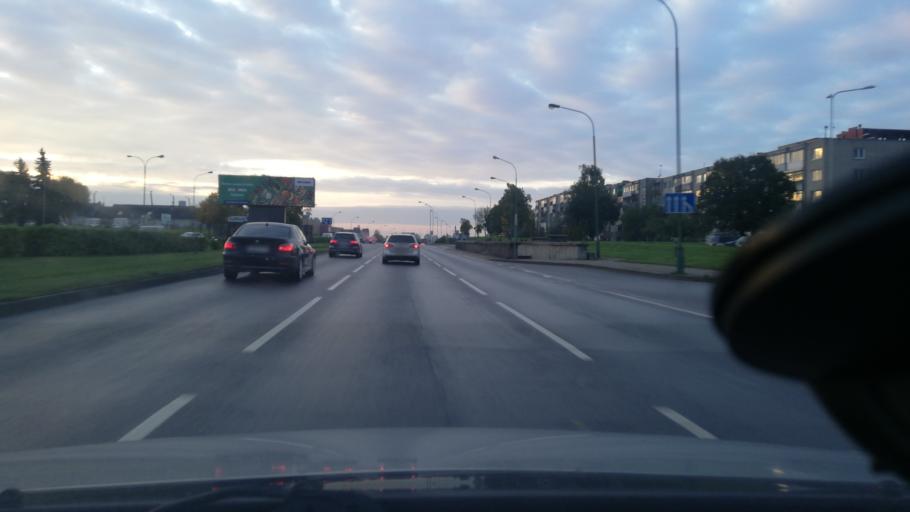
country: LT
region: Klaipedos apskritis
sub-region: Klaipeda
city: Klaipeda
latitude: 55.6893
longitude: 21.1807
